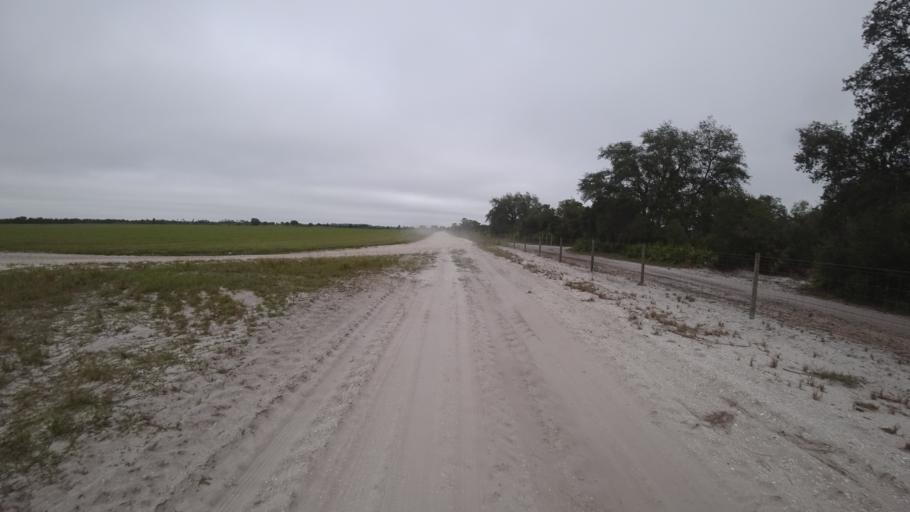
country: US
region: Florida
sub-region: Sarasota County
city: Warm Mineral Springs
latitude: 27.2870
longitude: -82.1346
